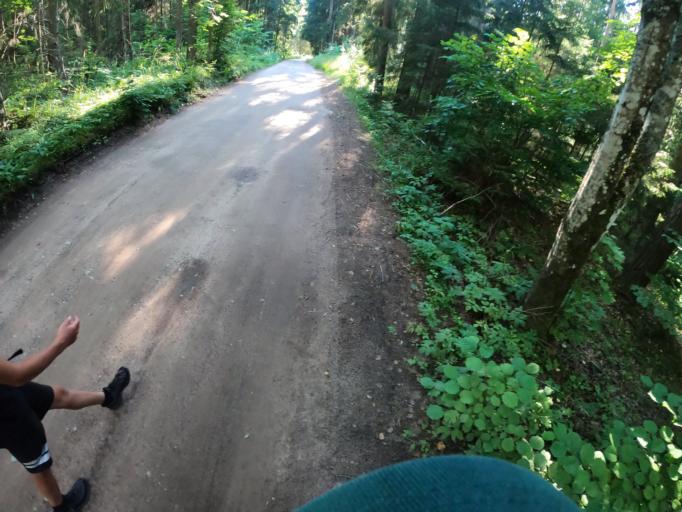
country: LT
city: Kursenai
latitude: 55.8225
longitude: 22.9342
